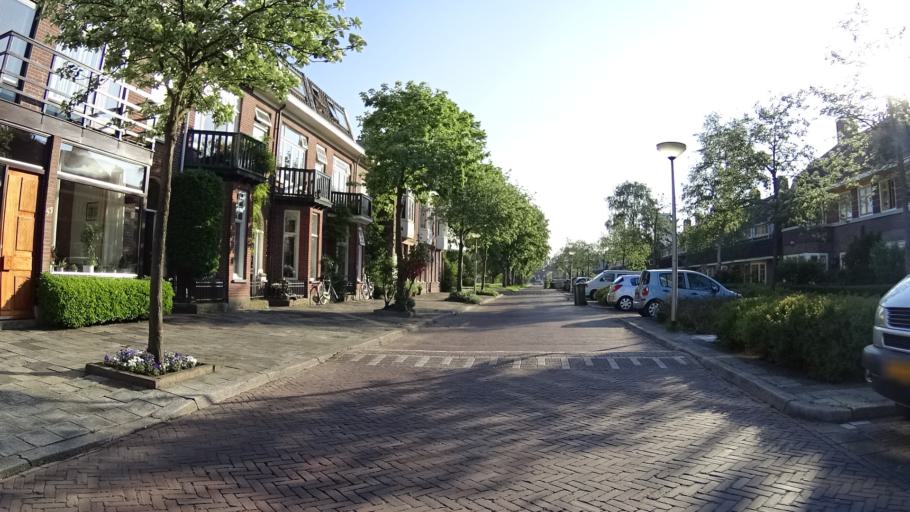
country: NL
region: South Holland
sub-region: Gemeente Delft
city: Delft
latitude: 52.0149
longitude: 4.3461
